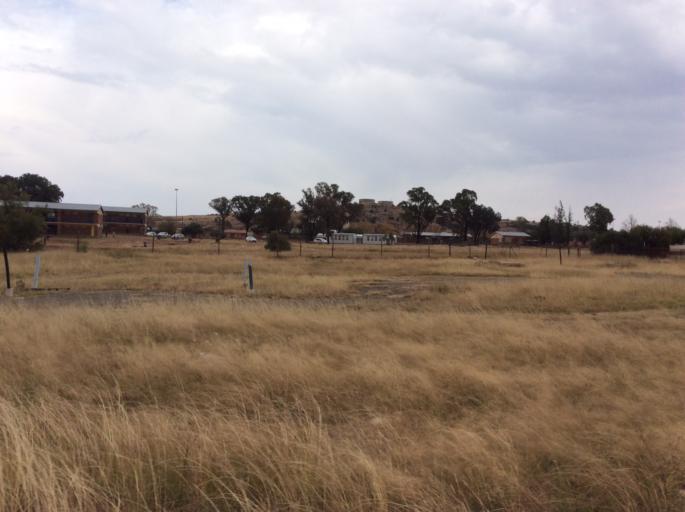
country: ZA
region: Orange Free State
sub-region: Xhariep District Municipality
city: Dewetsdorp
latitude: -29.5821
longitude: 26.6756
